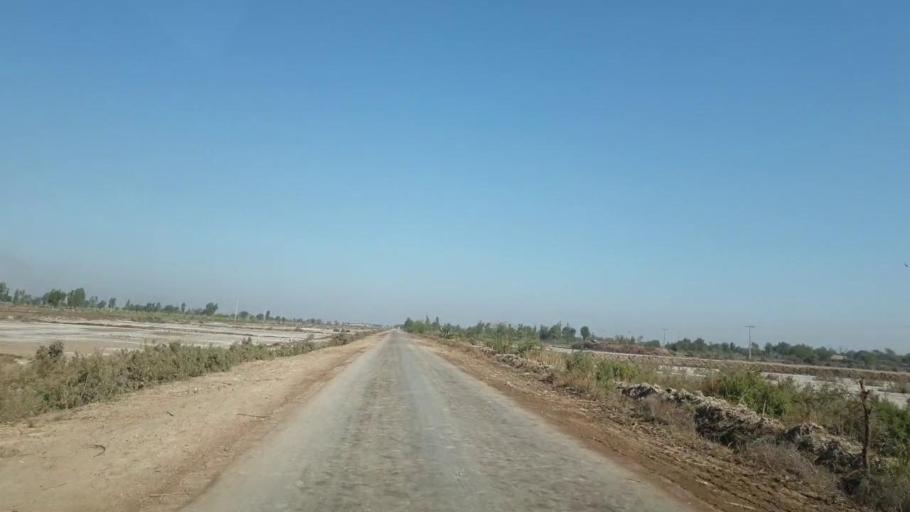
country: PK
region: Sindh
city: Mirpur Khas
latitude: 25.5834
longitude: 69.0457
